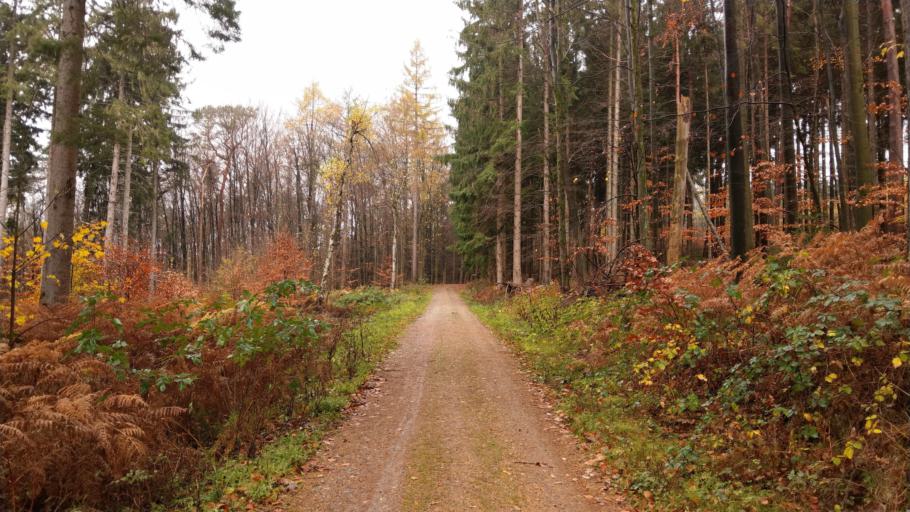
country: BE
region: Wallonia
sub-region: Province de Liege
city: La Calamine
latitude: 50.7334
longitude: 6.0516
